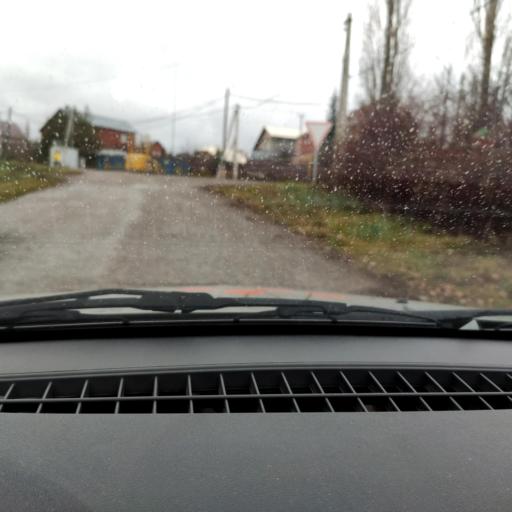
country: RU
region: Bashkortostan
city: Mikhaylovka
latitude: 54.8157
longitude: 55.8962
